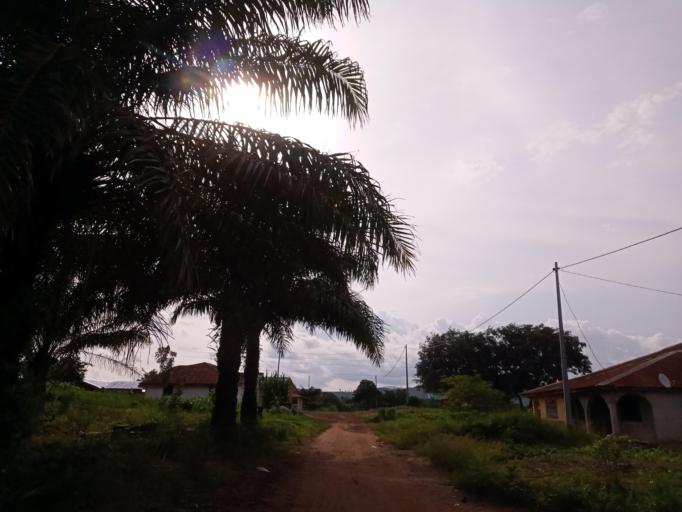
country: SL
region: Northern Province
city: Bumbuna
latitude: 9.0446
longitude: -11.7560
